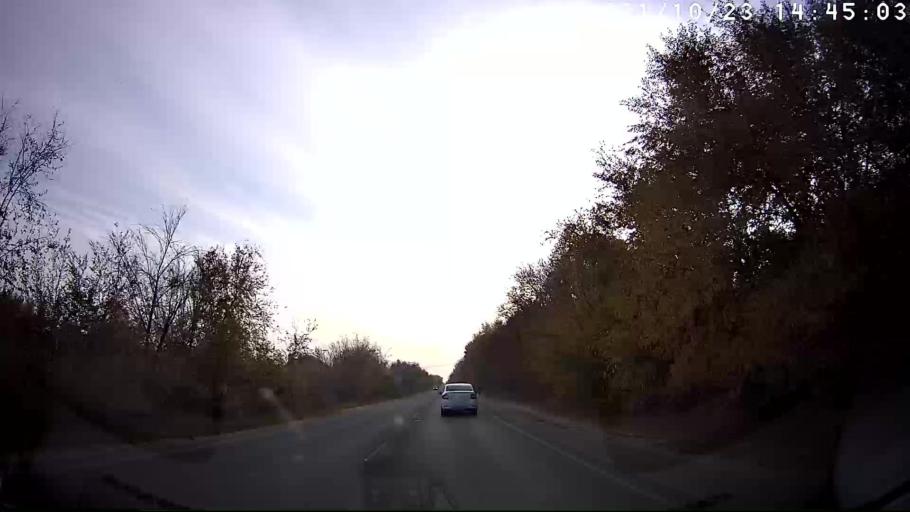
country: RU
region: Volgograd
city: Krasnoslobodsk
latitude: 48.4479
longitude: 44.5151
